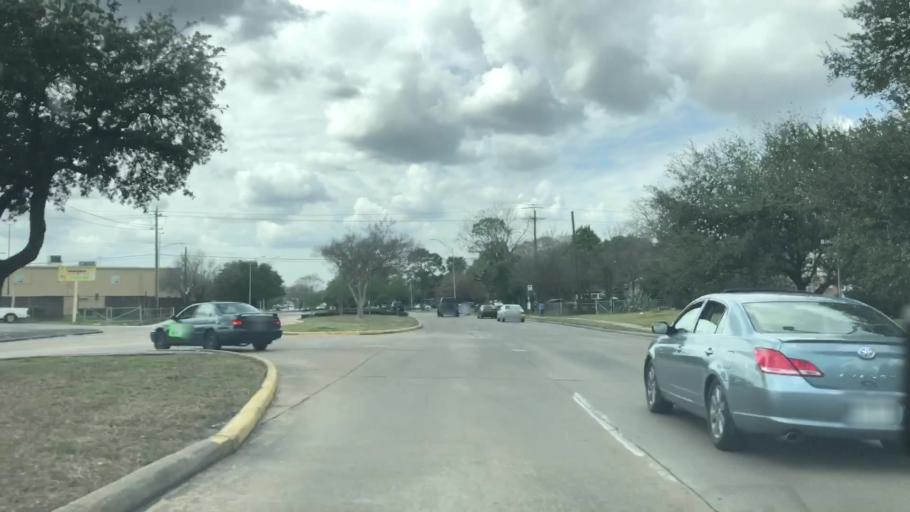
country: US
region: Texas
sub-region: Harris County
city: Bellaire
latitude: 29.6917
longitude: -95.5059
